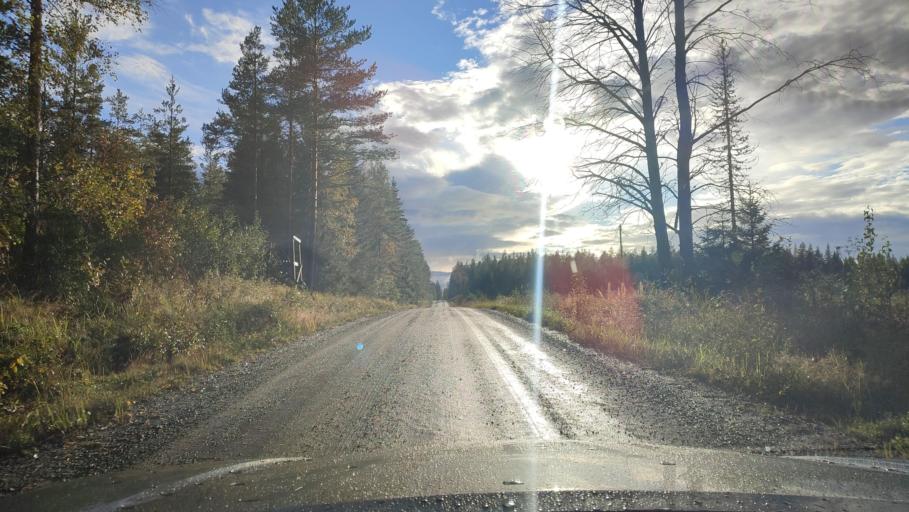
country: FI
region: Southern Ostrobothnia
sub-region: Suupohja
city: Karijoki
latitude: 62.3082
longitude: 21.5419
